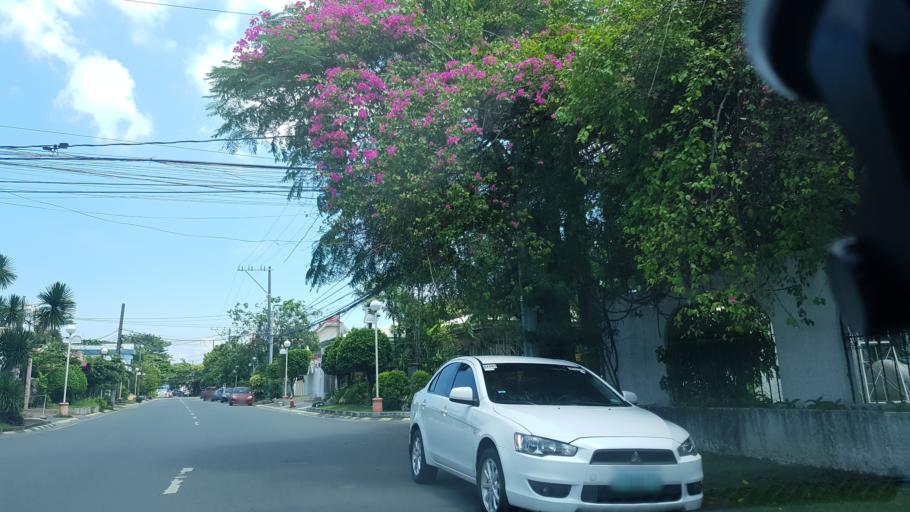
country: PH
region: Calabarzon
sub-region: Province of Rizal
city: Las Pinas
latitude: 14.4369
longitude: 120.9846
